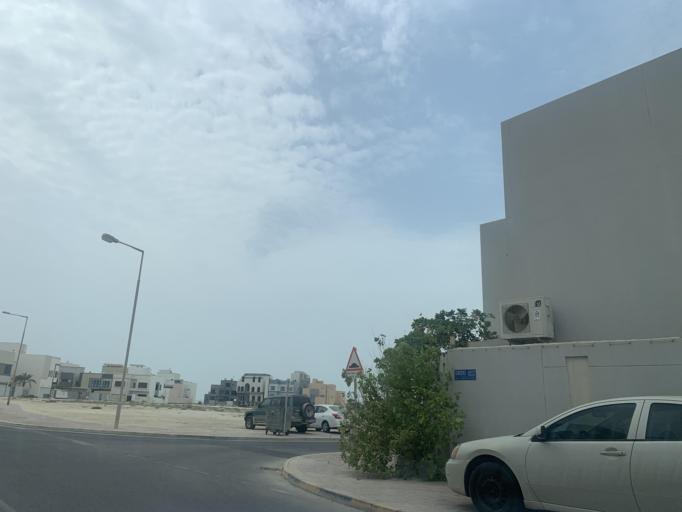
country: BH
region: Muharraq
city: Al Muharraq
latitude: 26.2849
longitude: 50.6378
